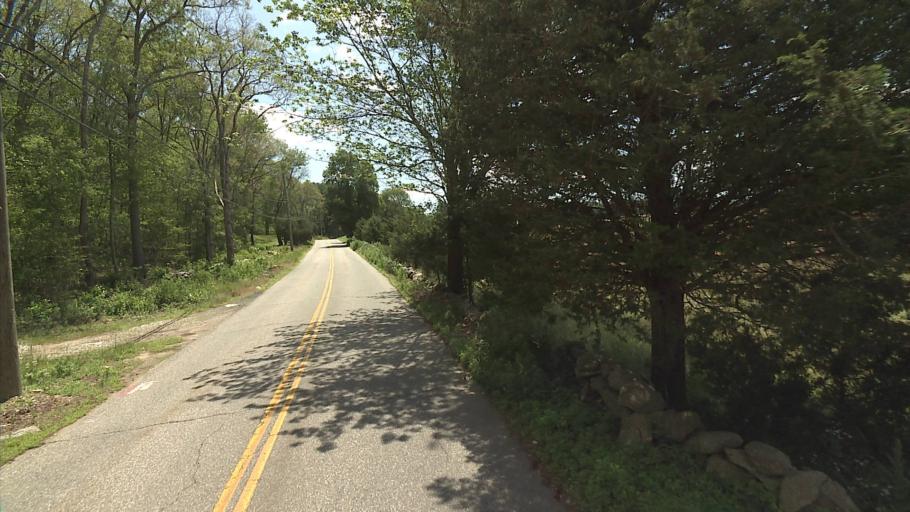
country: US
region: Connecticut
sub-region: New London County
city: Preston City
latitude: 41.5412
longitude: -71.8816
